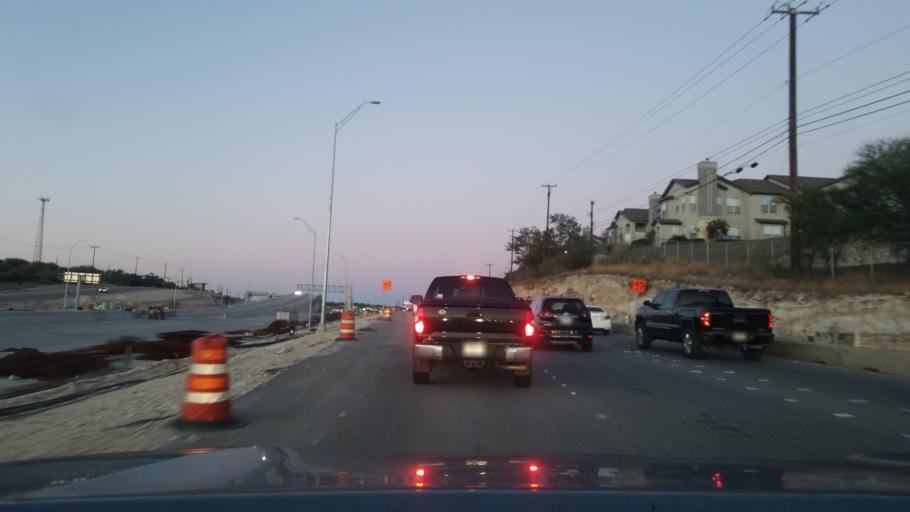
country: US
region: Texas
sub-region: Bexar County
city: Hollywood Park
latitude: 29.6416
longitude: -98.4534
